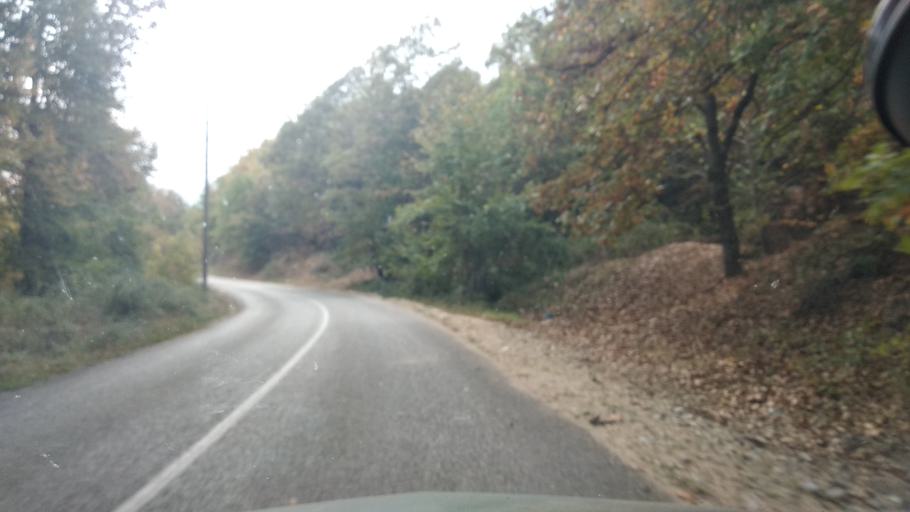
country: GR
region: Thessaly
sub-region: Trikala
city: Kastraki
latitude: 39.6901
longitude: 21.5176
